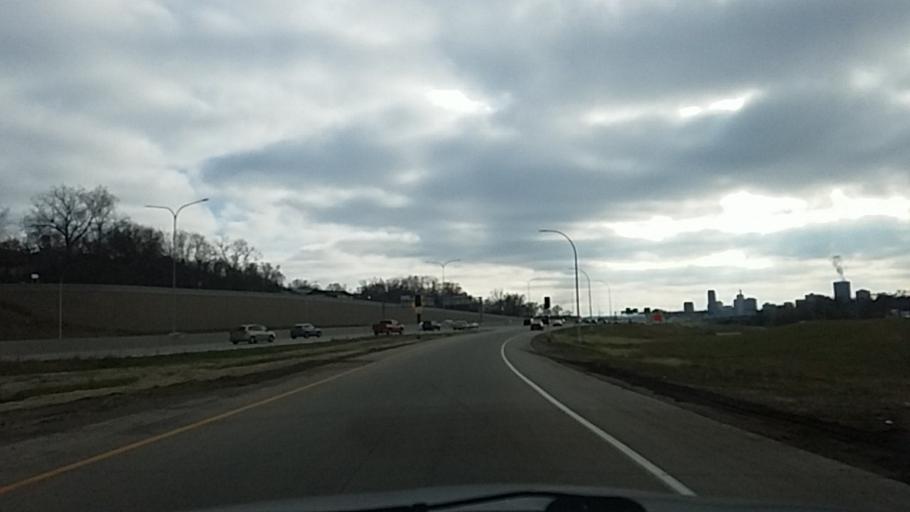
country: US
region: Minnesota
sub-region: Ramsey County
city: Saint Paul
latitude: 44.9755
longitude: -93.0894
